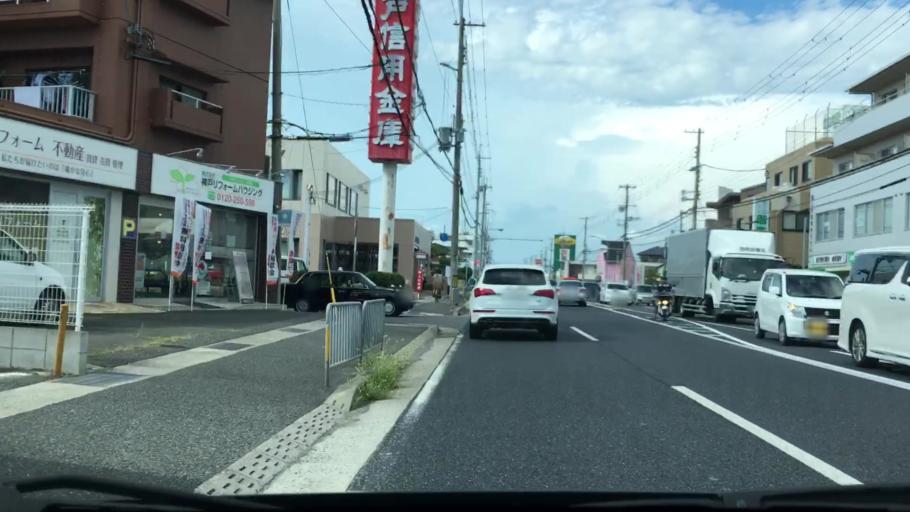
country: JP
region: Hyogo
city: Akashi
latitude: 34.6728
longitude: 134.9815
